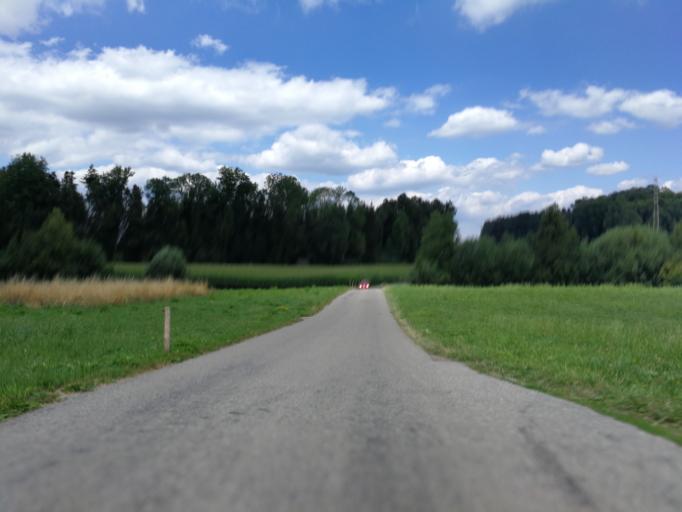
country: CH
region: Zurich
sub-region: Bezirk Hinwil
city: Wolfhausen
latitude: 47.2724
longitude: 8.7917
